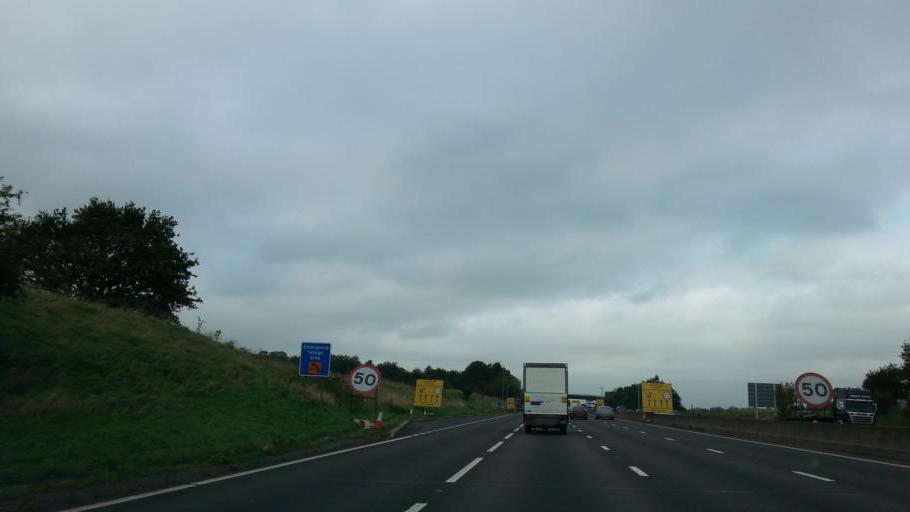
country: GB
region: England
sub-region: Staffordshire
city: Penkridge
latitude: 52.7463
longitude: -2.1000
